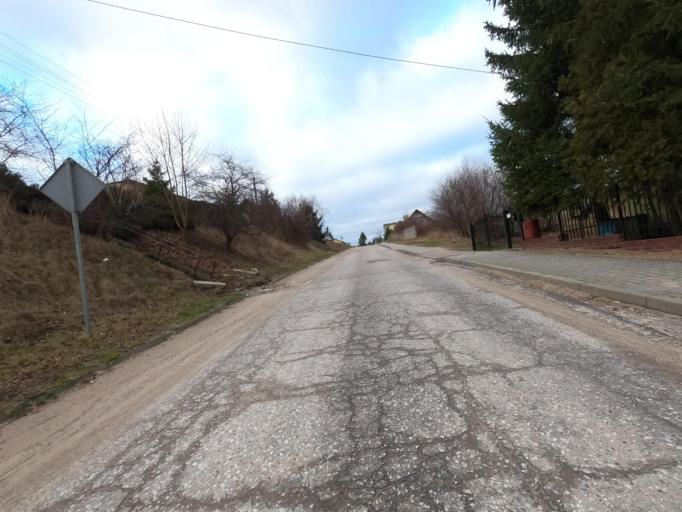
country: PL
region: Greater Poland Voivodeship
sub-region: Powiat pilski
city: Bialosliwie
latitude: 53.1005
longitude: 17.1219
